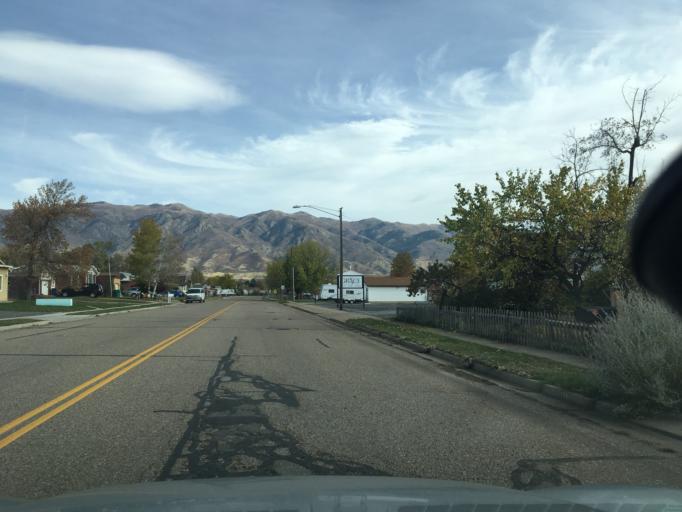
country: US
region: Utah
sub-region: Davis County
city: Layton
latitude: 41.0707
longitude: -111.9726
